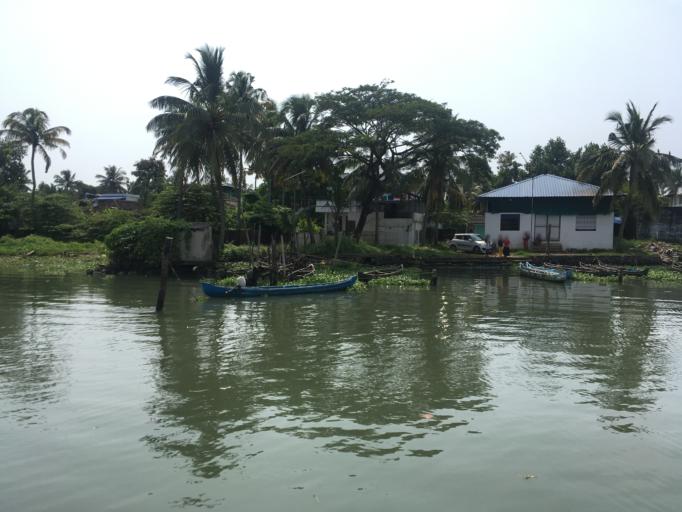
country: IN
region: Kerala
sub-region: Ernakulam
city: Cochin
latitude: 9.9774
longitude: 76.2428
